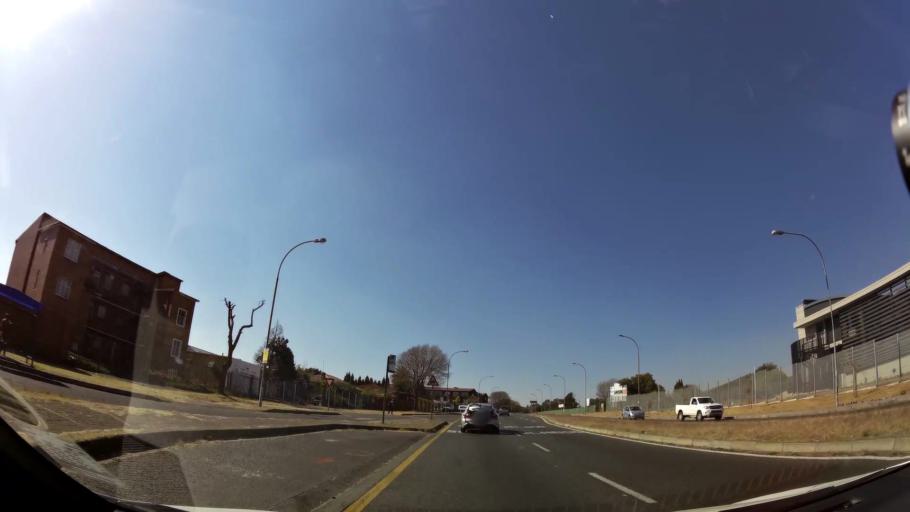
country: ZA
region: Gauteng
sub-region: City of Johannesburg Metropolitan Municipality
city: Johannesburg
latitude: -26.2605
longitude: 28.0328
